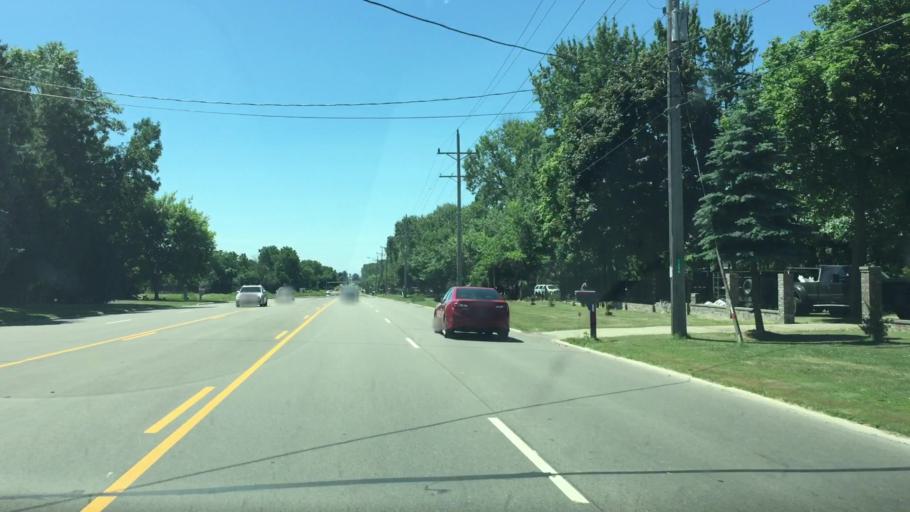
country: US
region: Wisconsin
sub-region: Outagamie County
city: Appleton
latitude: 44.2247
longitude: -88.4042
